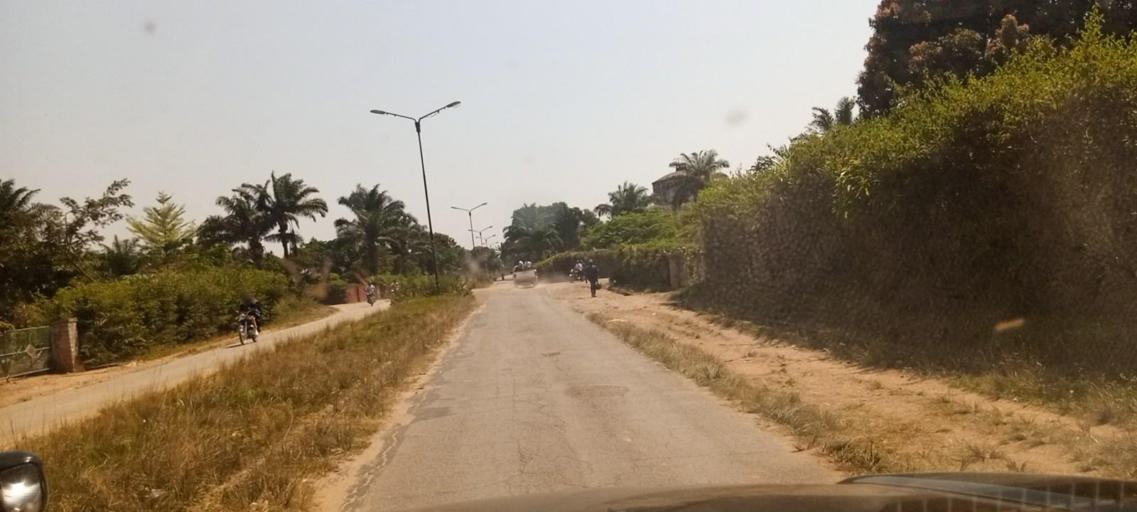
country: CD
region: Kasai-Oriental
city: Mbuji-Mayi
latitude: -6.1227
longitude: 23.5899
